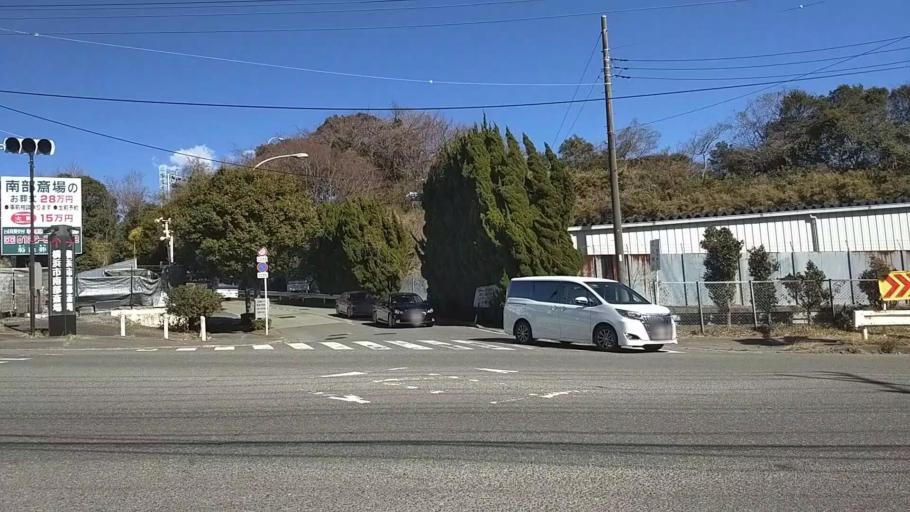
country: JP
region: Kanagawa
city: Zushi
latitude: 35.3329
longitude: 139.5915
